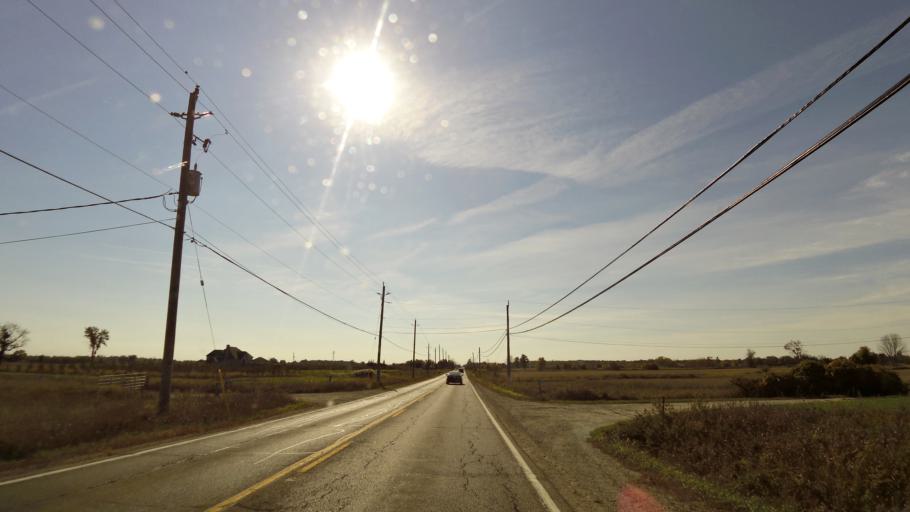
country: CA
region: Ontario
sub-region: Halton
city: Milton
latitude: 43.5423
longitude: -79.7736
